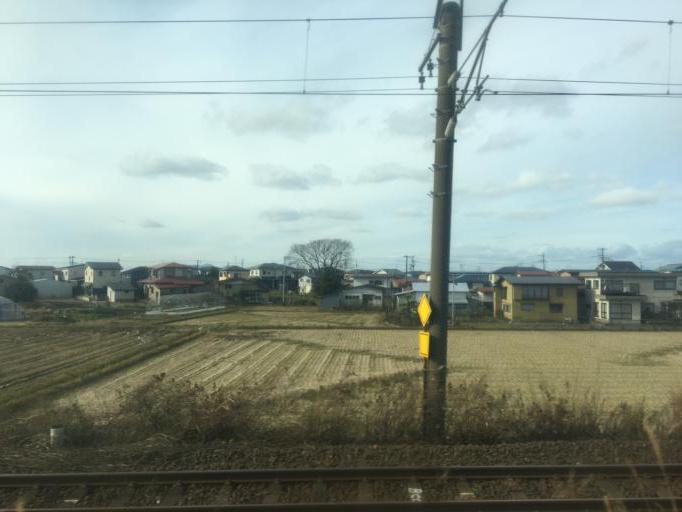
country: JP
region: Akita
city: Tenno
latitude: 39.9372
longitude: 140.0795
